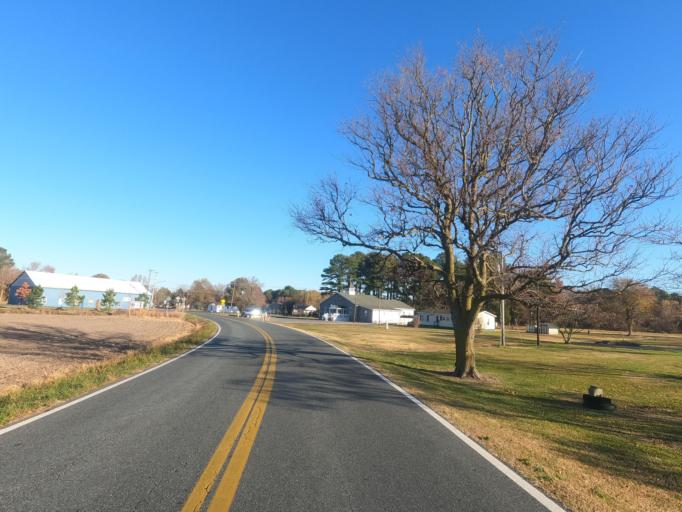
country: US
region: Maryland
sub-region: Somerset County
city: Crisfield
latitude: 38.0091
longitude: -75.8155
